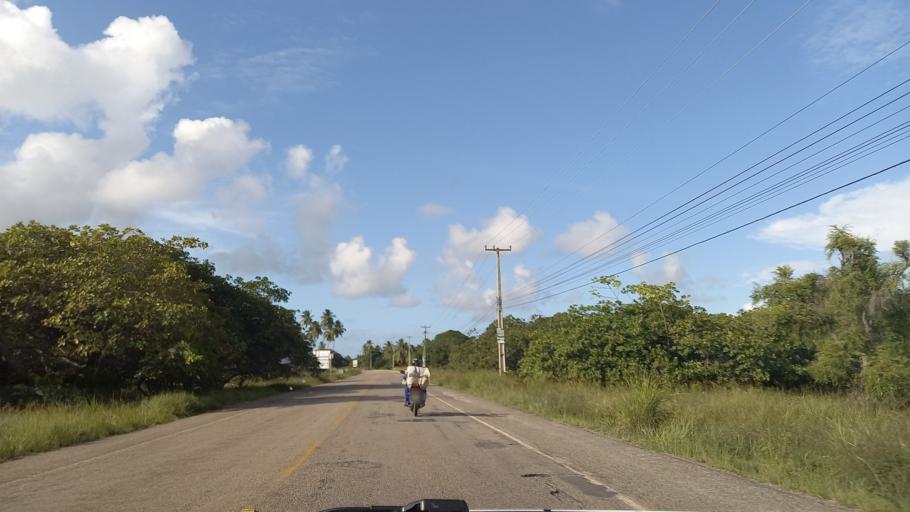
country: BR
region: Pernambuco
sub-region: Tamandare
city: Tamandare
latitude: -8.7130
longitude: -35.0915
